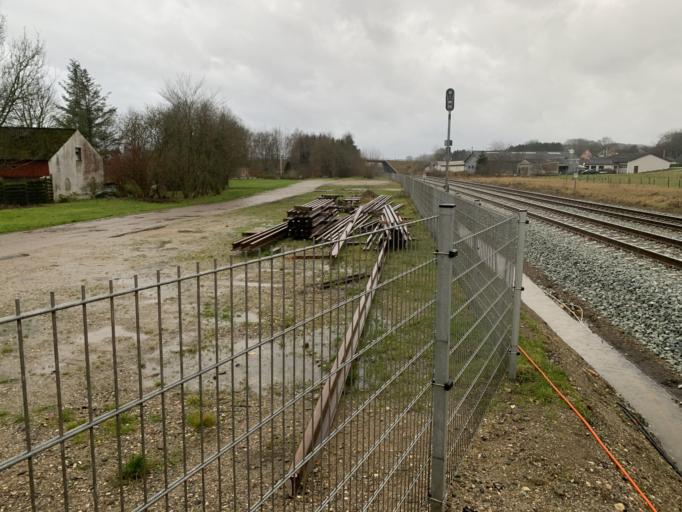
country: DK
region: North Denmark
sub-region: Alborg Kommune
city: Svenstrup
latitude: 56.9293
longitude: 9.8701
